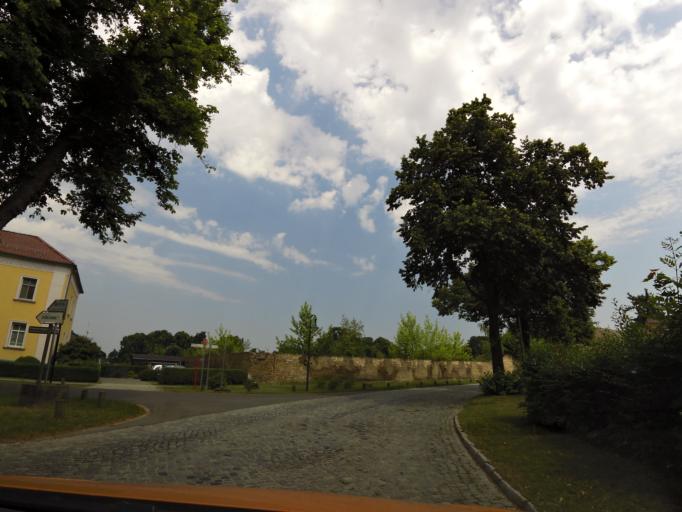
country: DE
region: Brandenburg
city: Nauen
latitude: 52.5780
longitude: 12.8717
